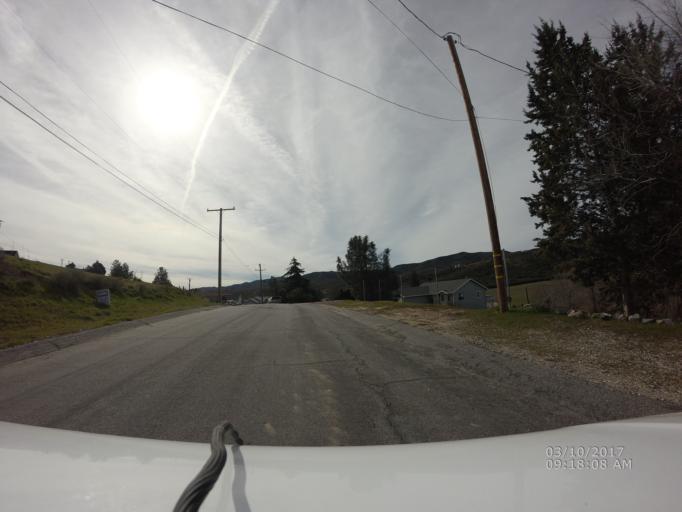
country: US
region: California
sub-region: Los Angeles County
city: Green Valley
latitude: 34.6582
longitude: -118.3905
